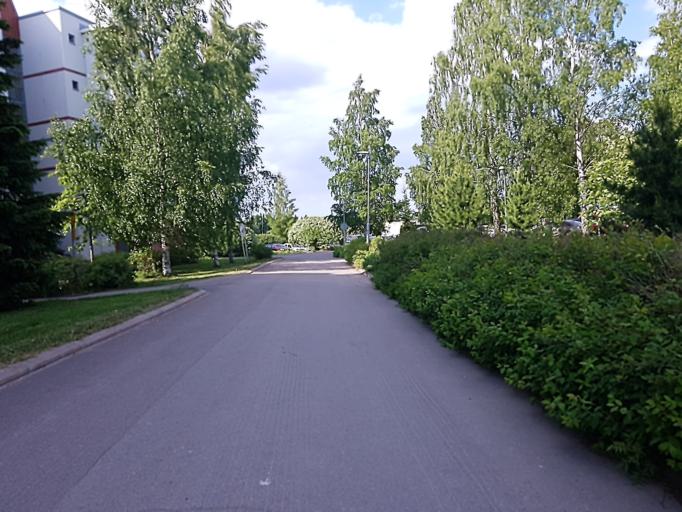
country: FI
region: Uusimaa
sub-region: Helsinki
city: Helsinki
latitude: 60.2331
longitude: 24.9819
